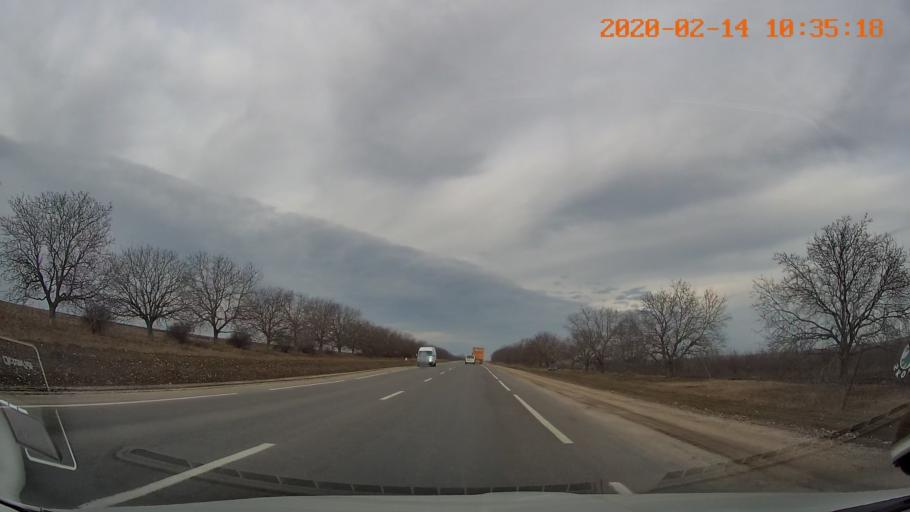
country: MD
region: Riscani
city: Riscani
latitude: 47.9133
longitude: 27.6548
